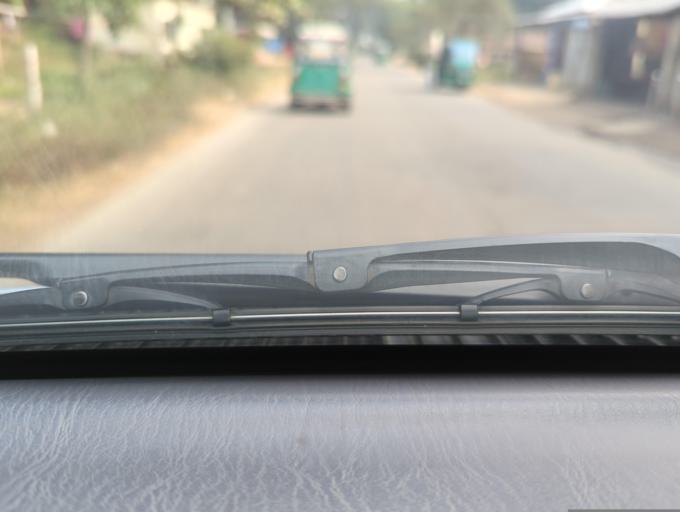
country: BD
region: Sylhet
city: Maulavi Bazar
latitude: 24.4970
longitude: 91.7427
